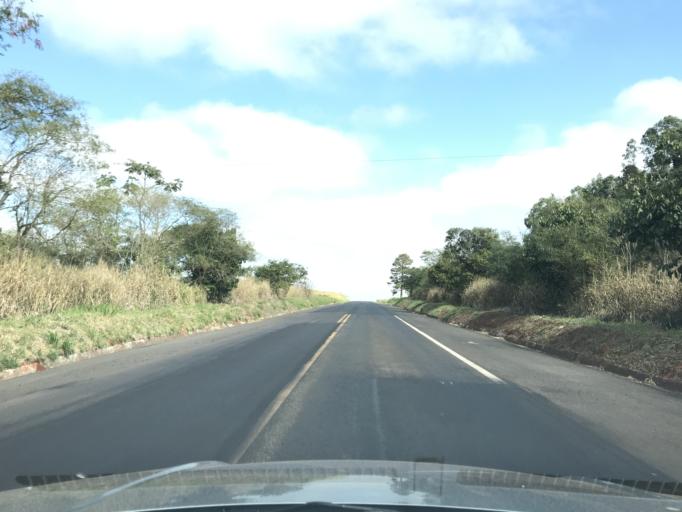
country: PY
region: Canindeyu
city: Salto del Guaira
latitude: -24.0785
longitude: -54.0604
